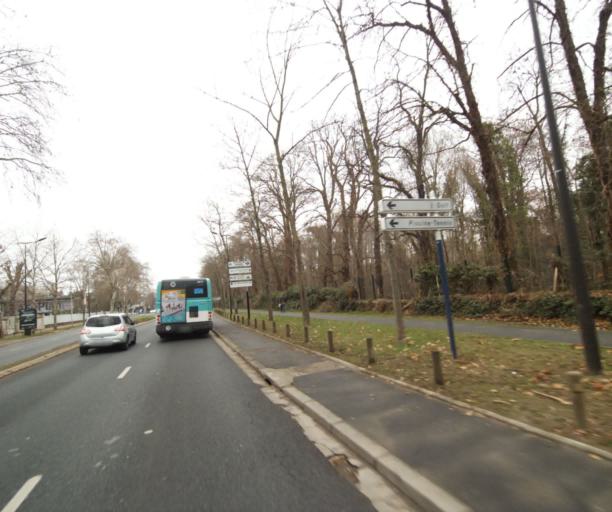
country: FR
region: Ile-de-France
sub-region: Departement des Yvelines
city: Chatou
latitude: 48.8738
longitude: 2.1658
